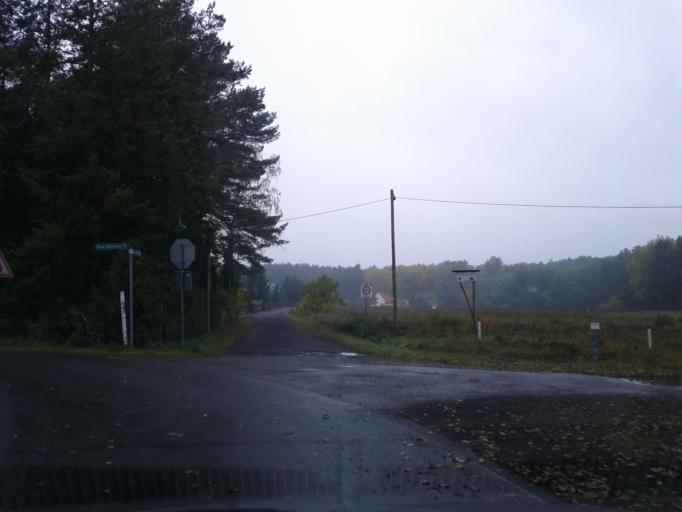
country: DE
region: Brandenburg
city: Spreenhagen
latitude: 52.3890
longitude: 13.8866
